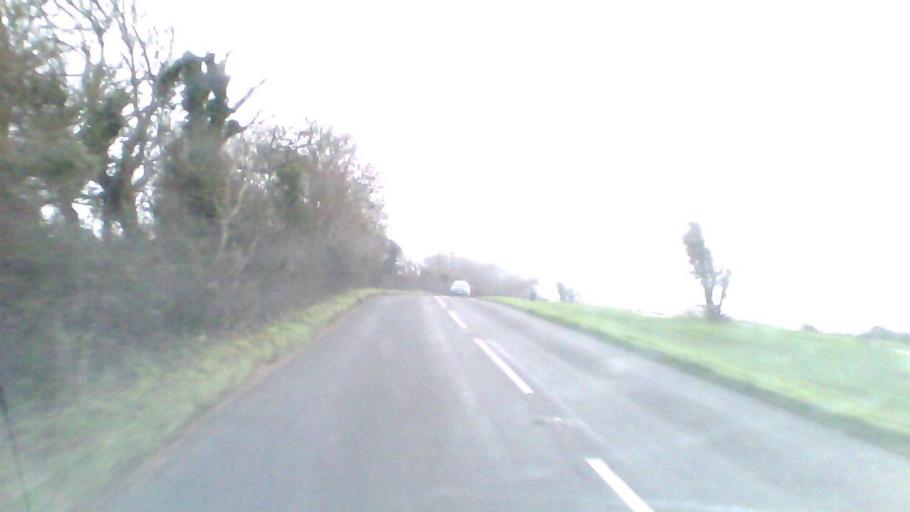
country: GB
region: England
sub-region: Isle of Wight
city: Brading
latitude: 50.6790
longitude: -1.1557
